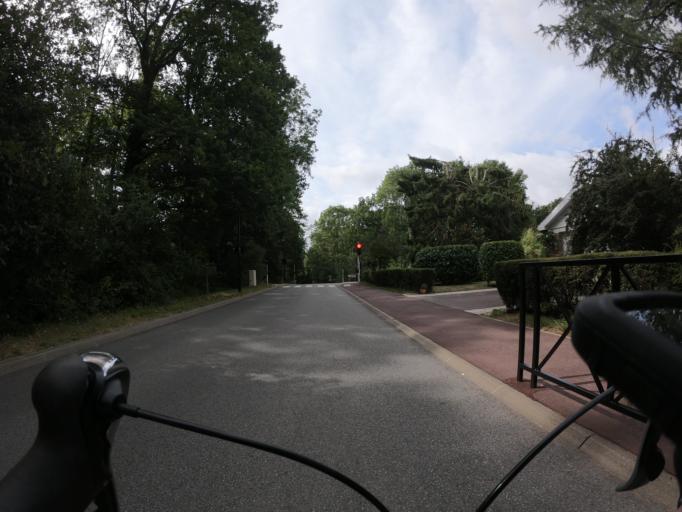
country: FR
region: Ile-de-France
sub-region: Departement des Yvelines
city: Voisins-le-Bretonneux
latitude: 48.7525
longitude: 2.0509
